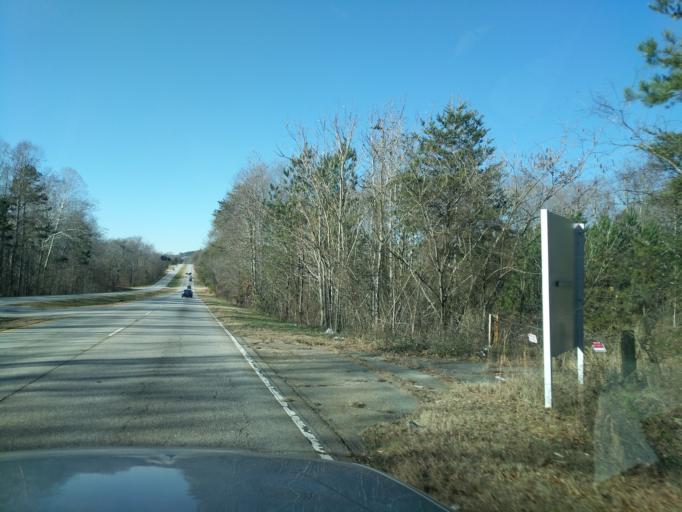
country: US
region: South Carolina
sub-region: Greenville County
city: Parker
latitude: 34.8336
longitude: -82.4651
